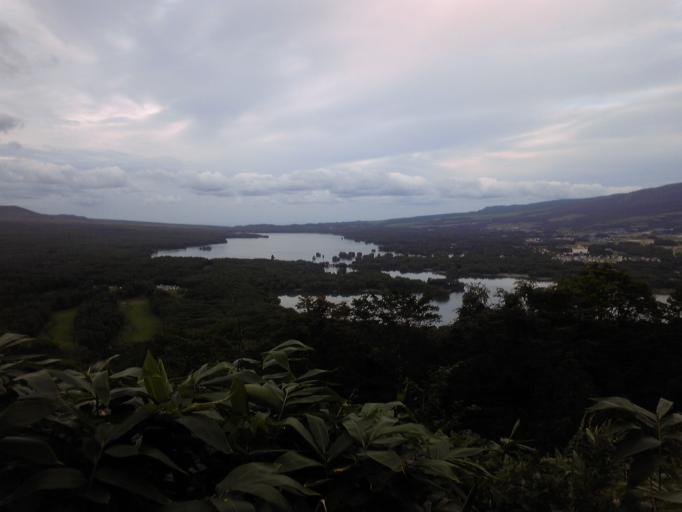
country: JP
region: Hokkaido
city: Nanae
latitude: 41.9808
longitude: 140.6438
